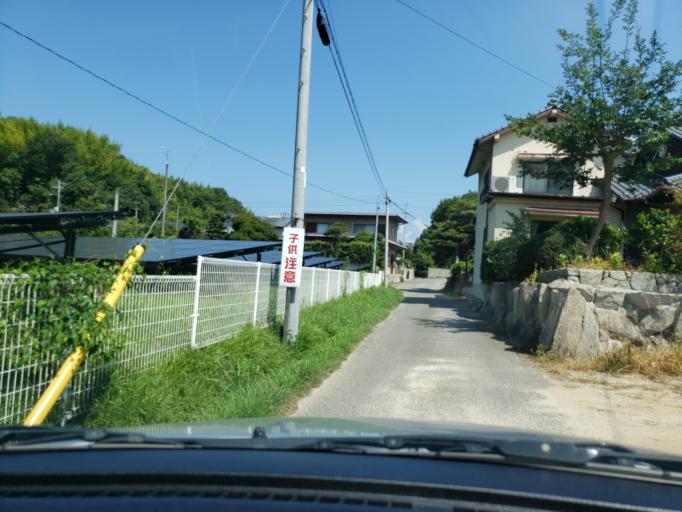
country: JP
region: Ehime
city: Hojo
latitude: 34.0859
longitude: 132.9294
